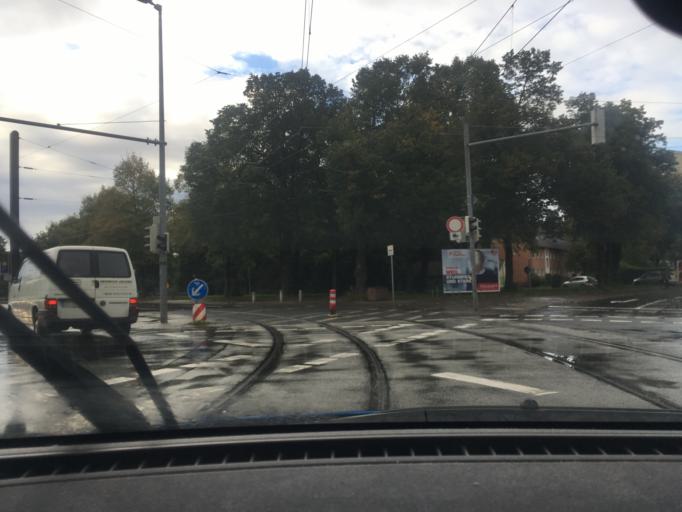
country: DE
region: Lower Saxony
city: Langenhagen
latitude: 52.4150
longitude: 9.7968
